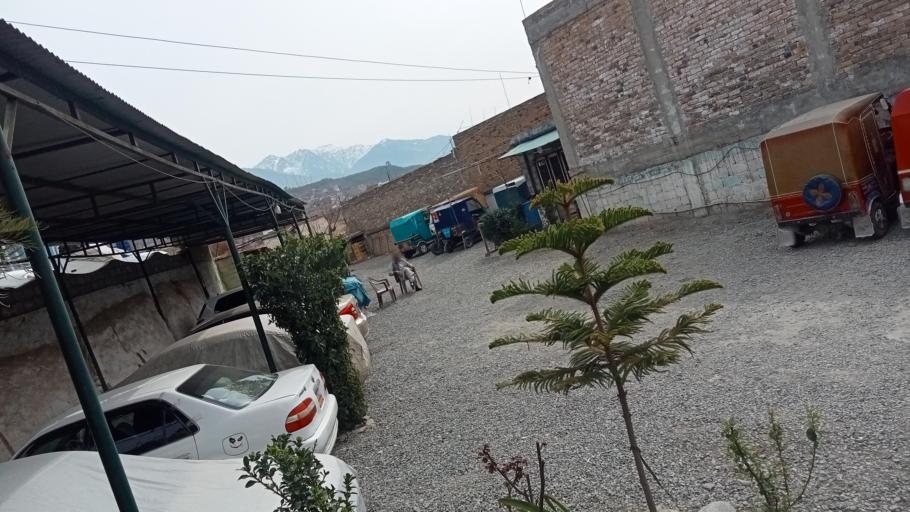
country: PK
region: Khyber Pakhtunkhwa
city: Mingora
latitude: 34.7708
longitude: 72.3693
